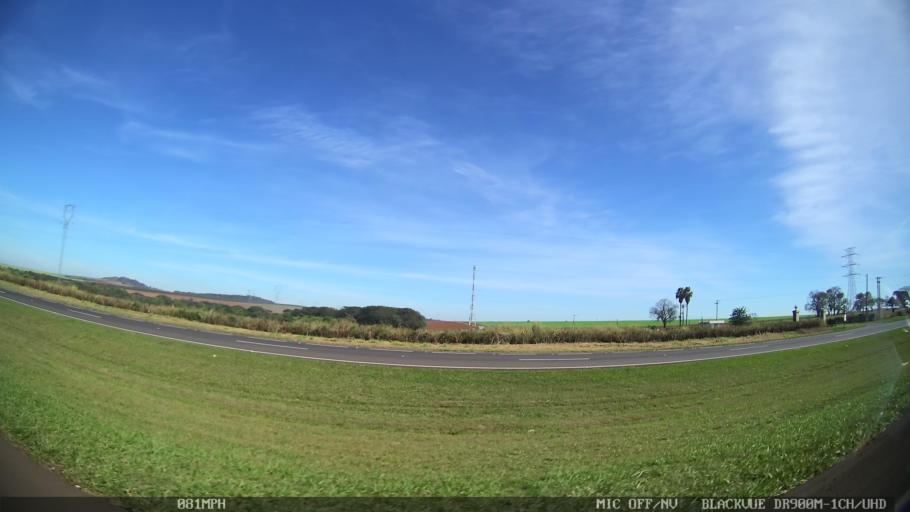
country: BR
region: Sao Paulo
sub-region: Araras
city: Araras
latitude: -22.2863
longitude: -47.3935
